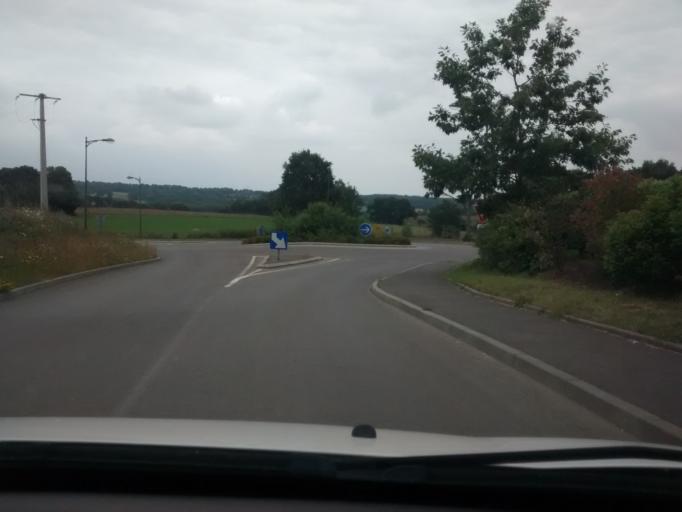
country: FR
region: Brittany
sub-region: Departement d'Ille-et-Vilaine
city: La Bouexiere
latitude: 48.1871
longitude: -1.4430
